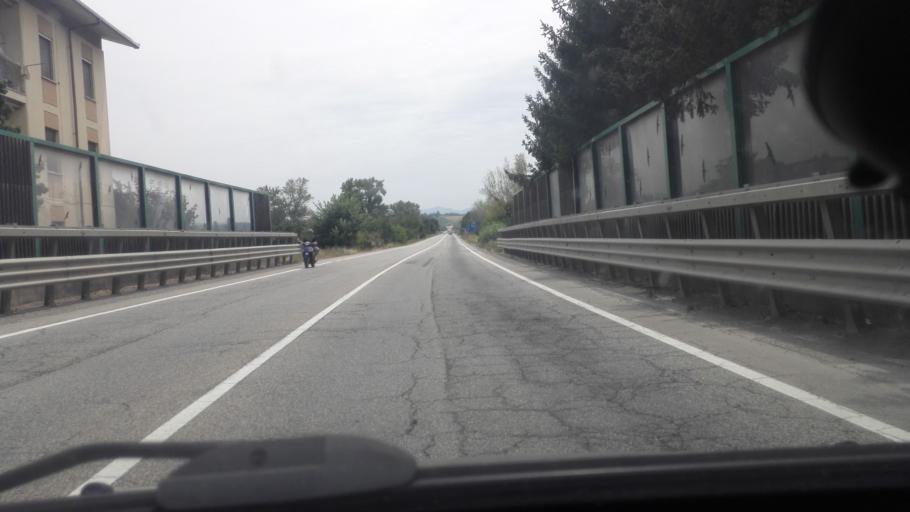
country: IT
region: Piedmont
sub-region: Provincia di Alessandria
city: Novi Ligure
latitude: 44.7656
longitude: 8.8062
